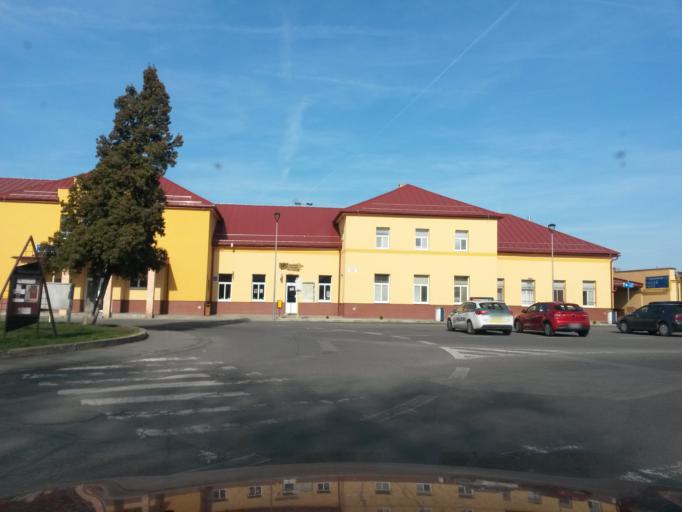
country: SK
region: Banskobystricky
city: Lucenec
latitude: 48.3354
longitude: 19.6673
